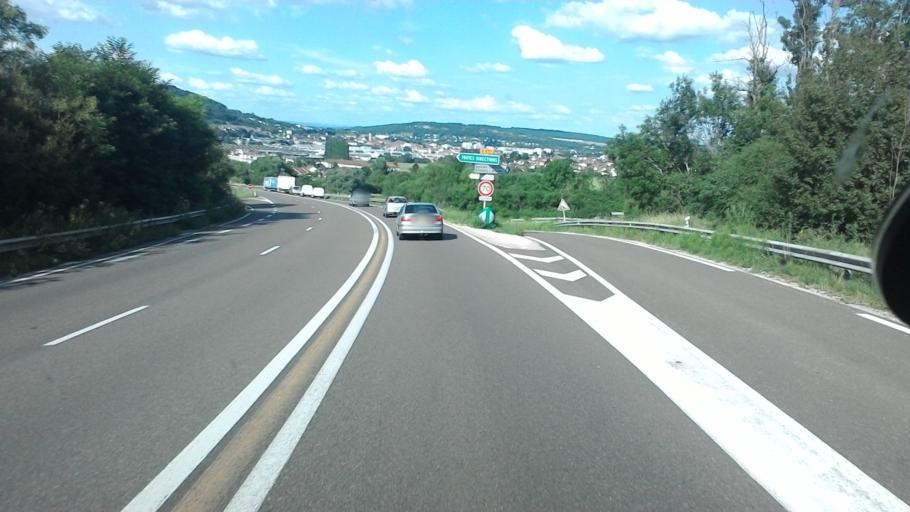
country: FR
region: Franche-Comte
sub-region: Departement de la Haute-Saone
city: Noidans-les-Vesoul
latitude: 47.6074
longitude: 6.1294
